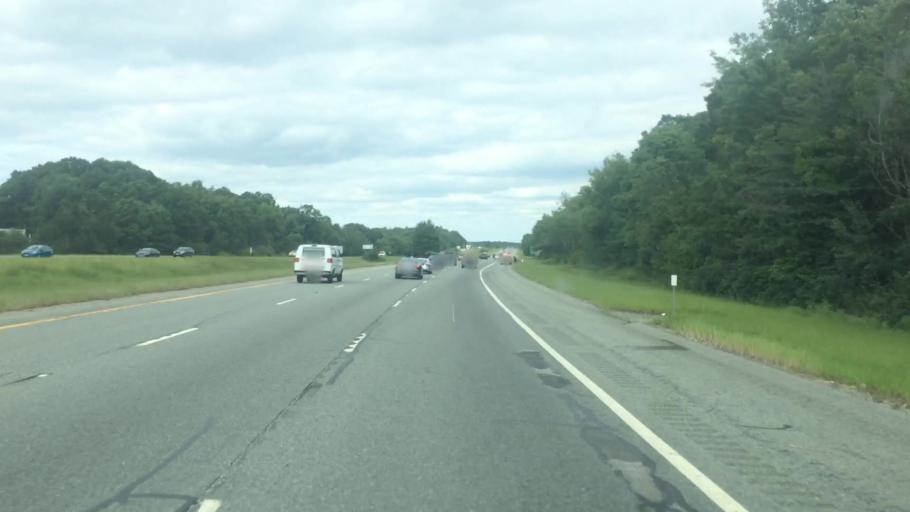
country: US
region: Rhode Island
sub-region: Providence County
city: Smithfield
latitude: 41.9318
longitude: -71.5000
